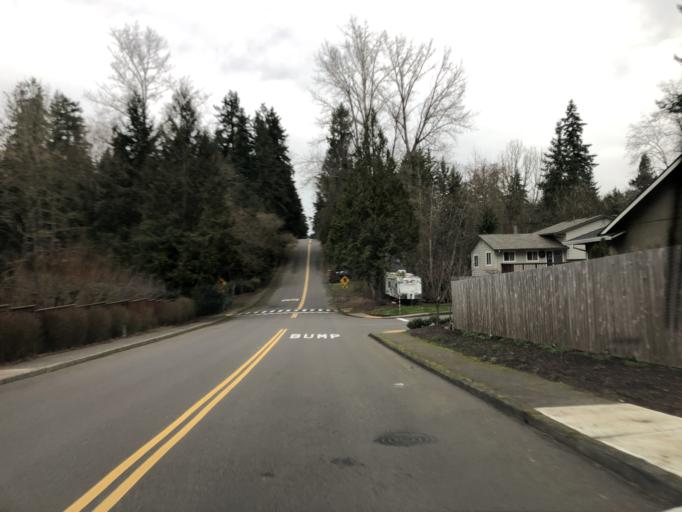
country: US
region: Oregon
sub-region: Washington County
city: King City
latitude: 45.4246
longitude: -122.7953
